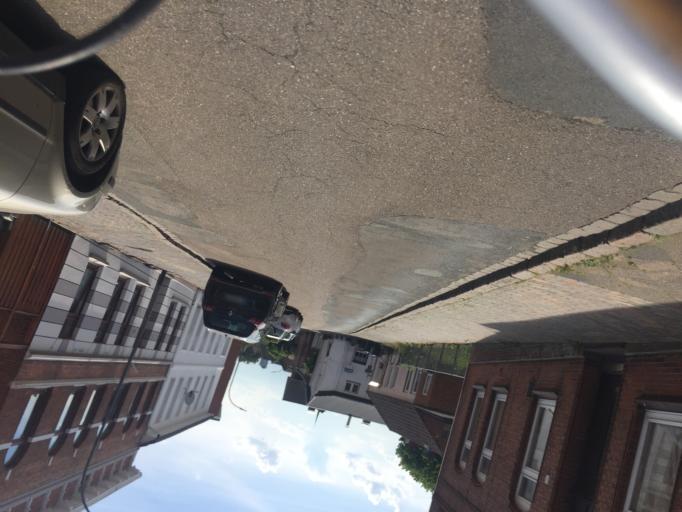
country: DE
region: Schleswig-Holstein
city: Itzehoe
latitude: 53.9277
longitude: 9.5241
